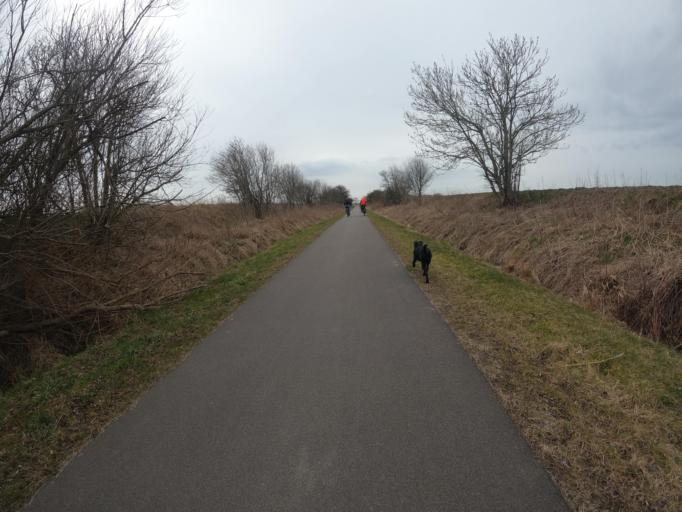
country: PL
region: West Pomeranian Voivodeship
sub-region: Powiat gryficki
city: Mrzezyno
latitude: 54.1153
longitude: 15.3018
